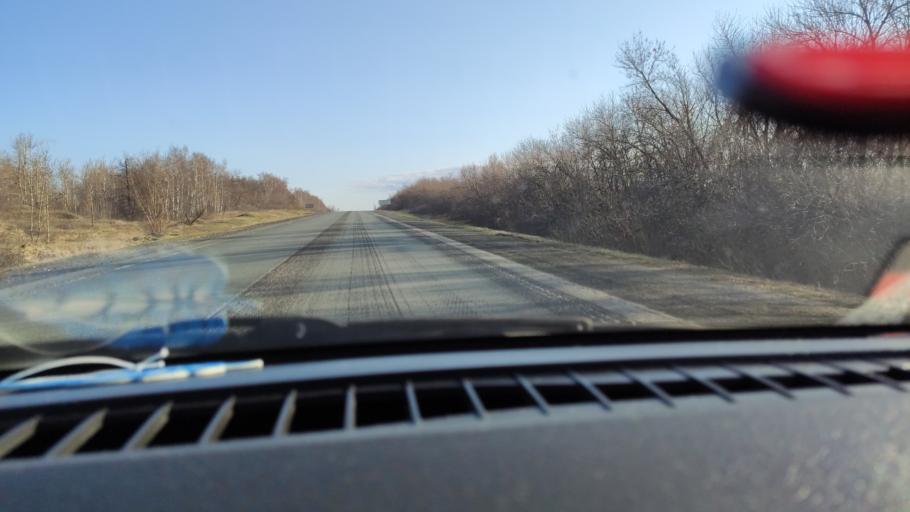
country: RU
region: Saratov
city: Dukhovnitskoye
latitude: 52.6337
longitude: 48.1862
